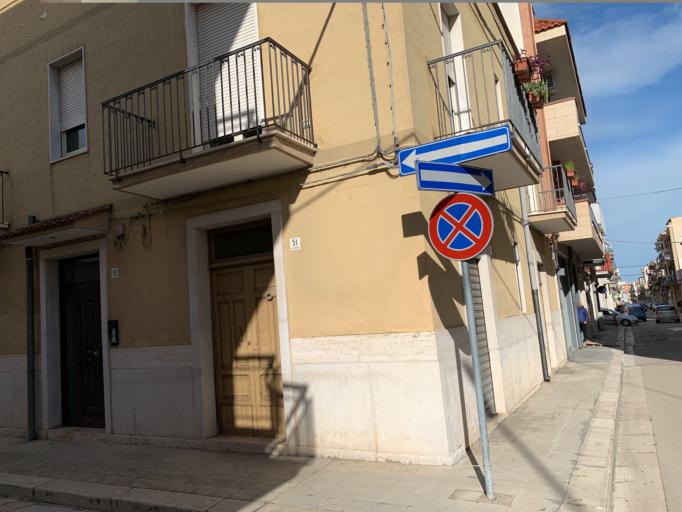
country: IT
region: Apulia
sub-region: Provincia di Barletta - Andria - Trani
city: Andria
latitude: 41.2318
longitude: 16.2932
